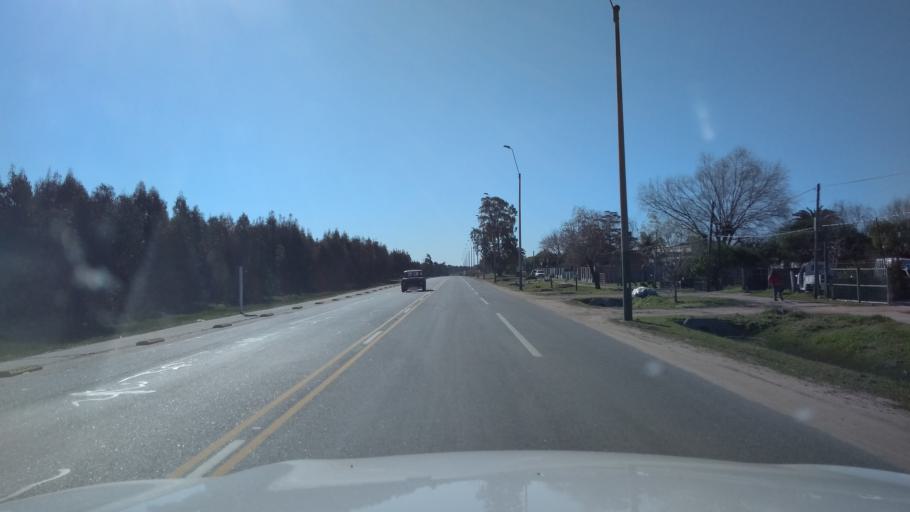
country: UY
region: Canelones
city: Atlantida
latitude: -34.7512
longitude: -55.7680
